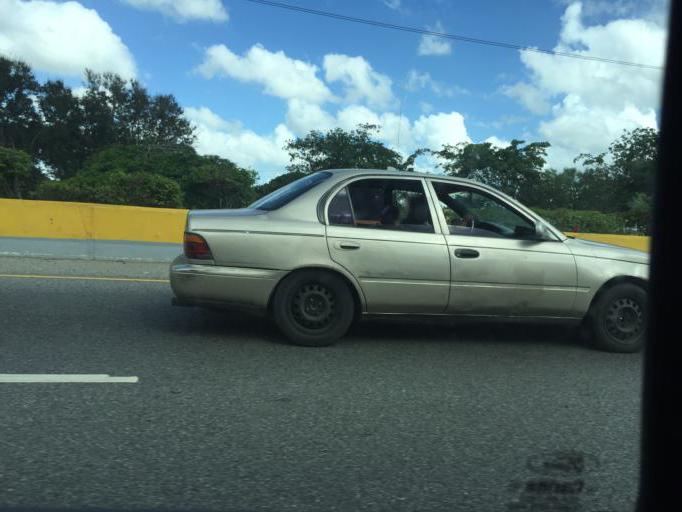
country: DO
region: Santo Domingo
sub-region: Santo Domingo
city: Santo Domingo Este
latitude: 18.4849
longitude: -69.8526
